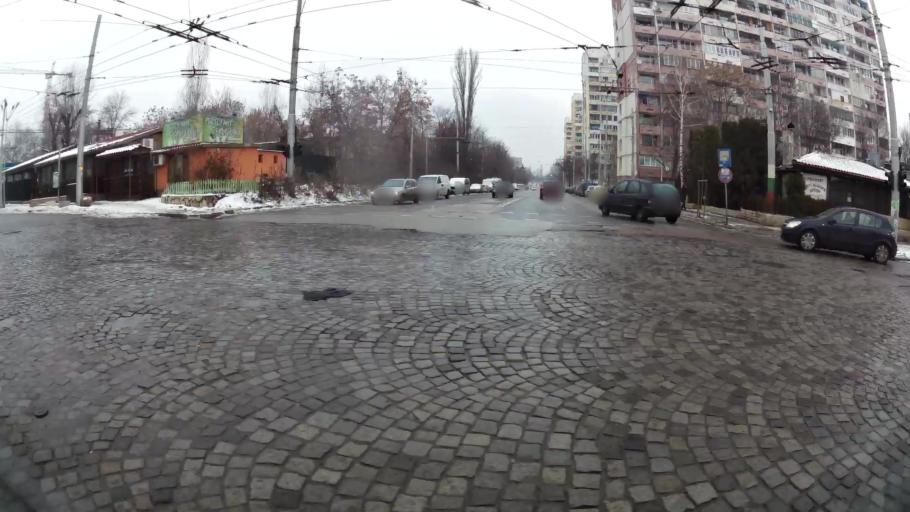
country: BG
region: Sofia-Capital
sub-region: Stolichna Obshtina
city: Sofia
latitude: 42.7109
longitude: 23.3097
